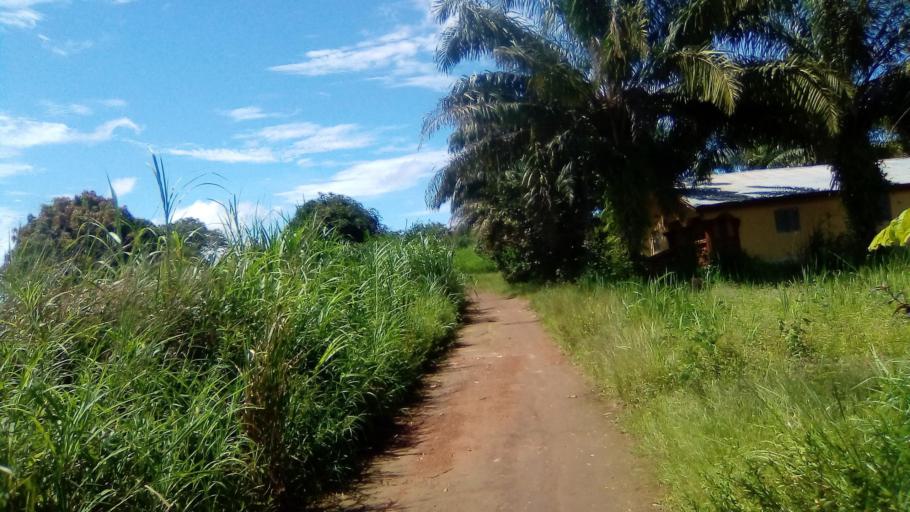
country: SL
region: Eastern Province
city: Simbakoro
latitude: 8.6307
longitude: -10.9988
